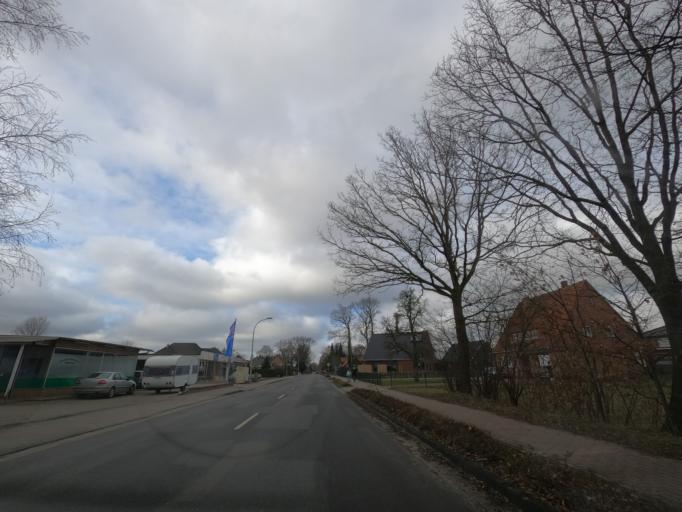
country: DE
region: Lower Saxony
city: Herzlake
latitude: 52.6861
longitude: 7.5993
